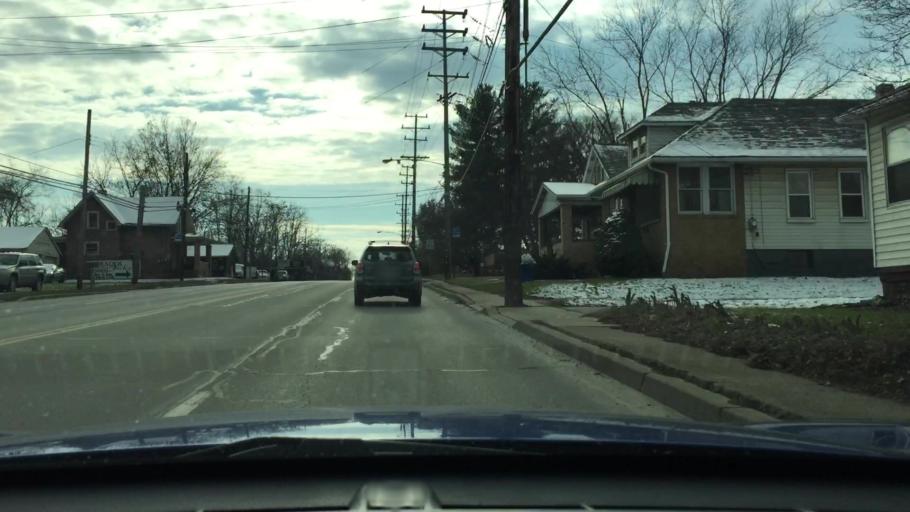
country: US
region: Pennsylvania
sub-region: Allegheny County
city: Heidelberg
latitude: 40.3767
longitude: -80.0977
